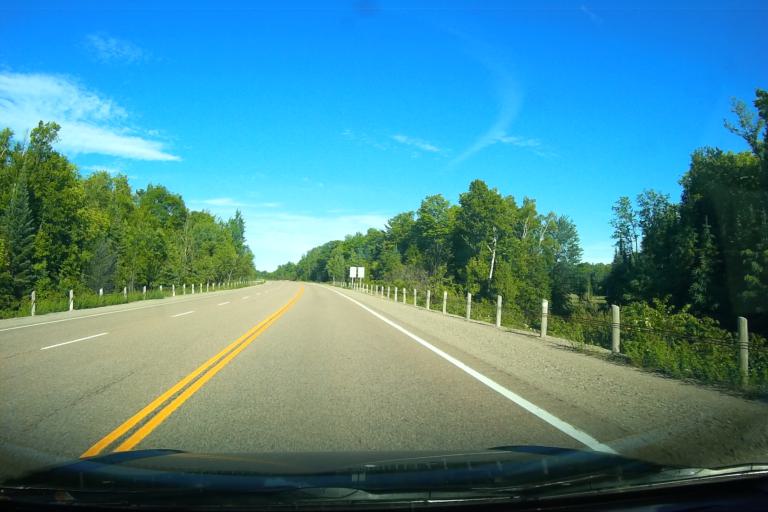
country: CA
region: Ontario
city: Pembroke
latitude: 45.7515
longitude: -77.0220
